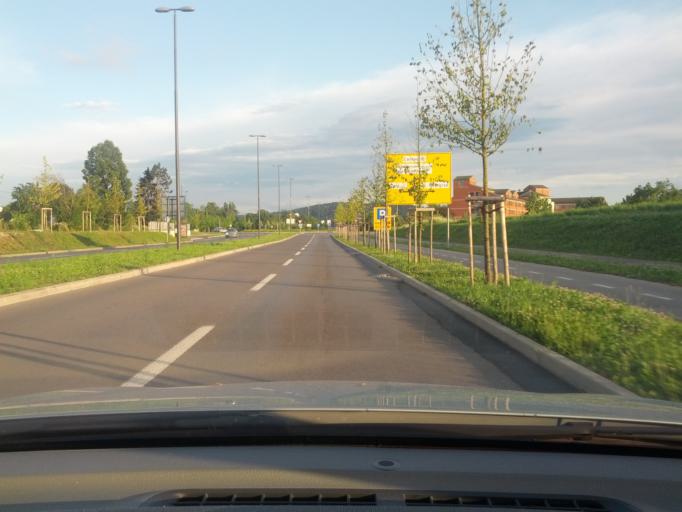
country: SI
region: Ljubljana
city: Ljubljana
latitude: 46.0716
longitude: 14.5252
